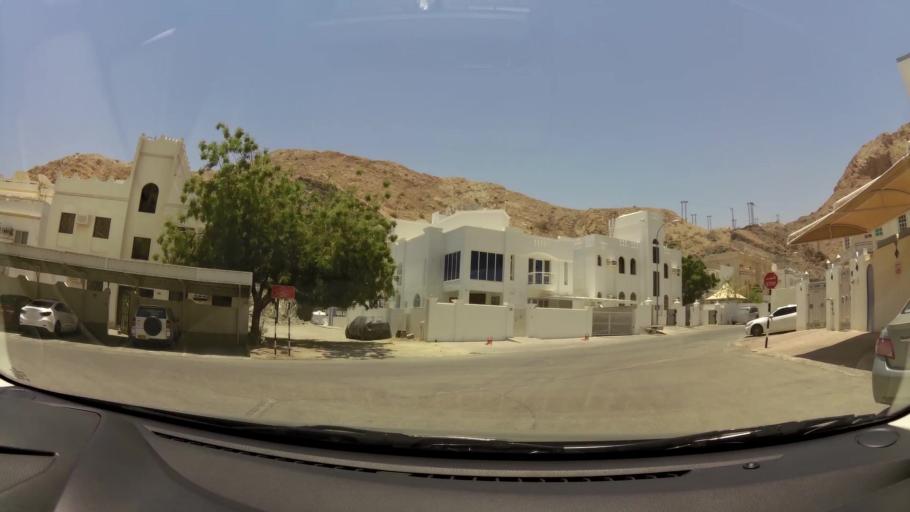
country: OM
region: Muhafazat Masqat
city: Muscat
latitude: 23.6143
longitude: 58.5336
